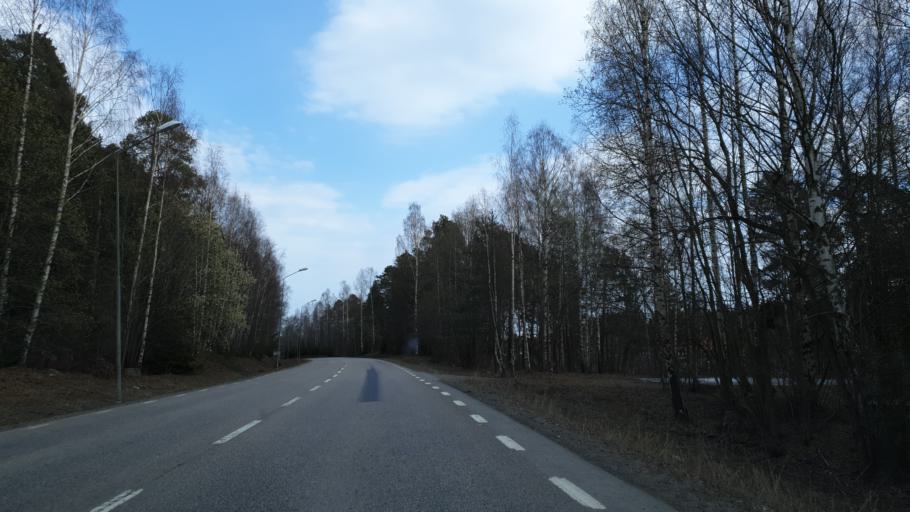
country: SE
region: Gaevleborg
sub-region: Hudiksvalls Kommun
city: Iggesund
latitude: 61.6420
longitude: 17.0657
